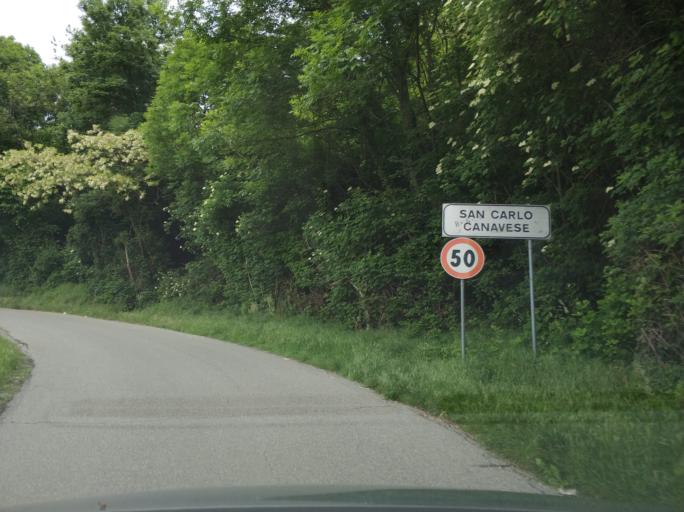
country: IT
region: Piedmont
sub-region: Provincia di Torino
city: San Carlo Canavese
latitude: 45.2510
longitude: 7.5889
